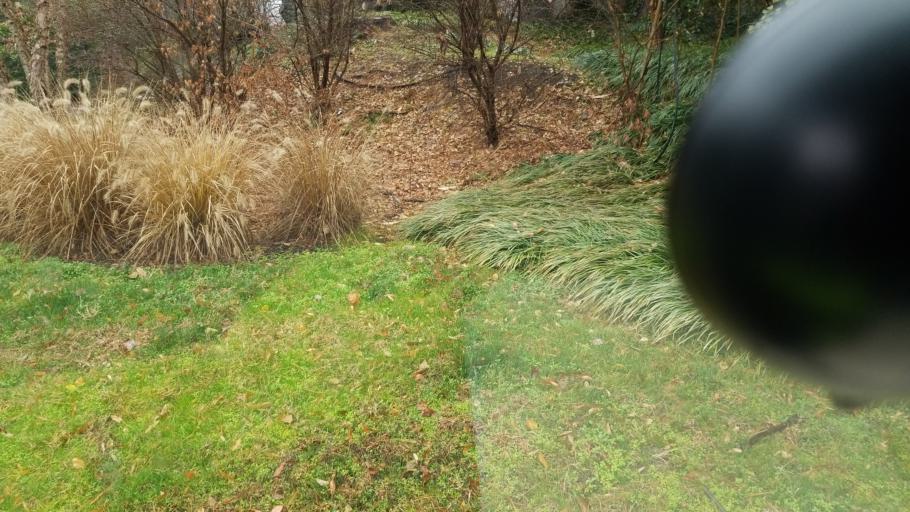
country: US
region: Maryland
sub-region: Montgomery County
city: Brookmont
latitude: 38.9280
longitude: -77.0980
